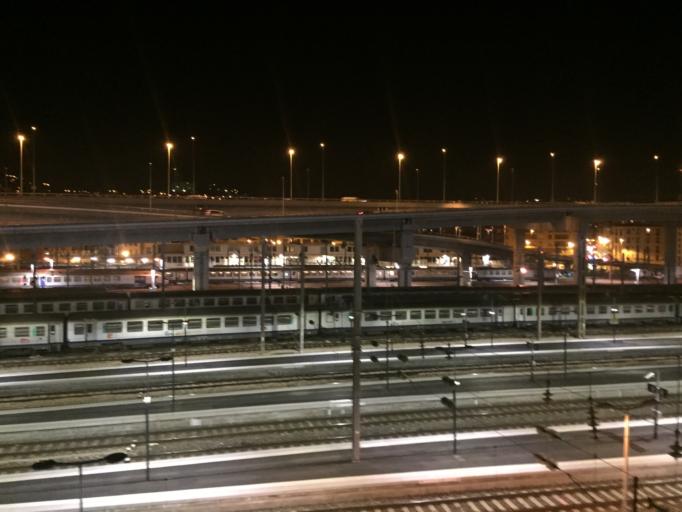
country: FR
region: Provence-Alpes-Cote d'Azur
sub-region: Departement des Alpes-Maritimes
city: Nice
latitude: 43.7038
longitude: 7.2593
